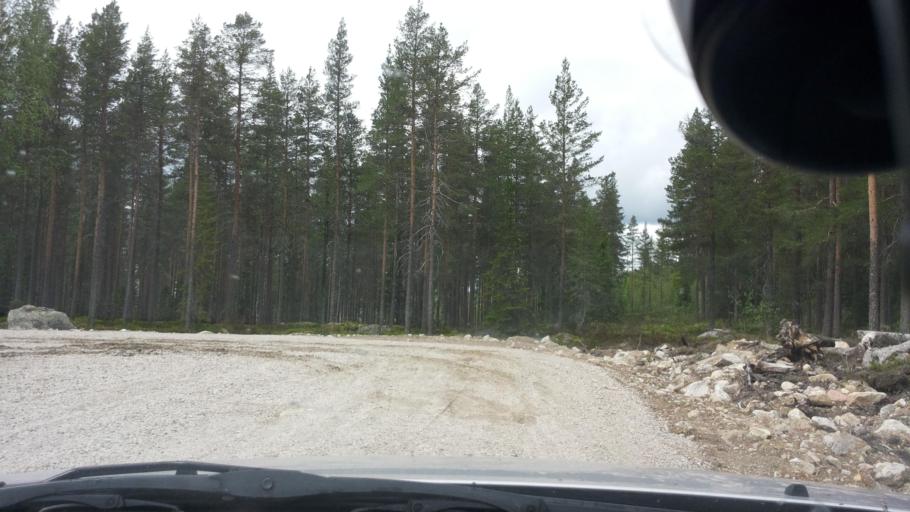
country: SE
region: Gaevleborg
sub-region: Ovanakers Kommun
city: Edsbyn
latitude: 61.4667
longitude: 15.2853
